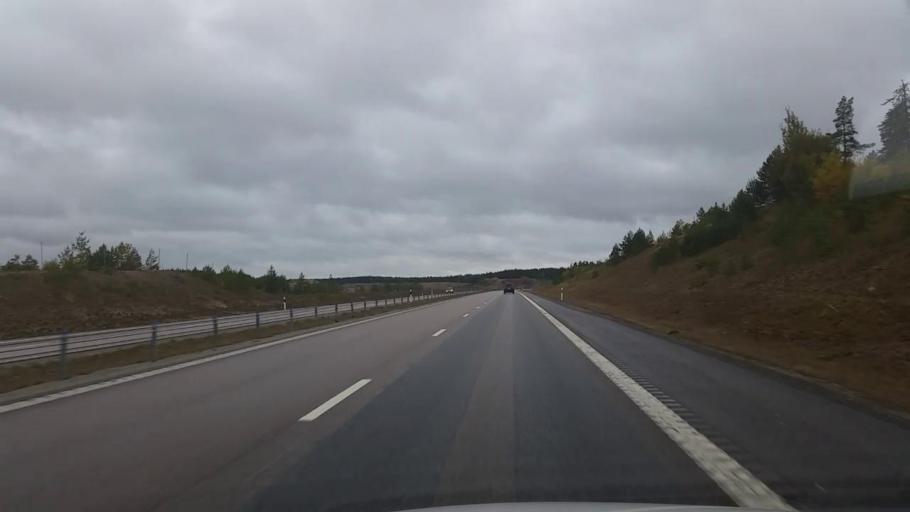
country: SE
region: Uppsala
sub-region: Osthammars Kommun
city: Bjorklinge
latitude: 60.1117
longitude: 17.5546
